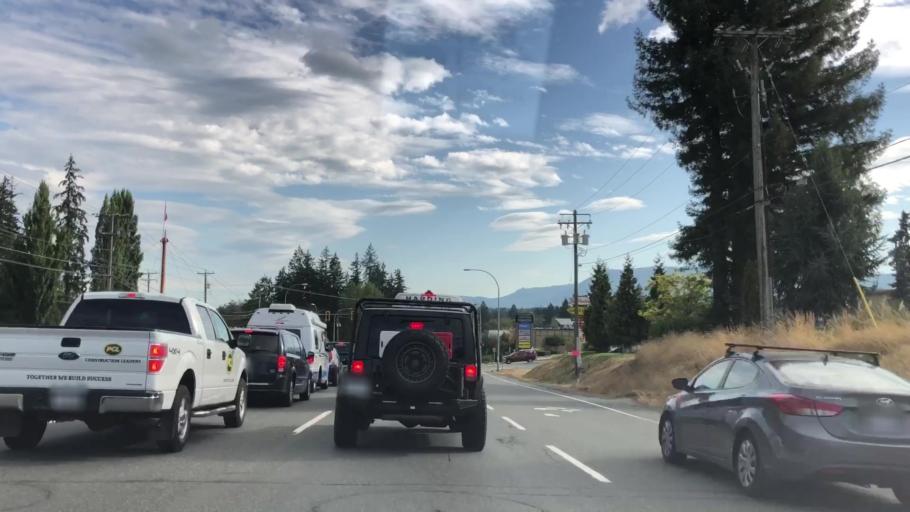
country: CA
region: British Columbia
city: Duncan
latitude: 48.8043
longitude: -123.7165
